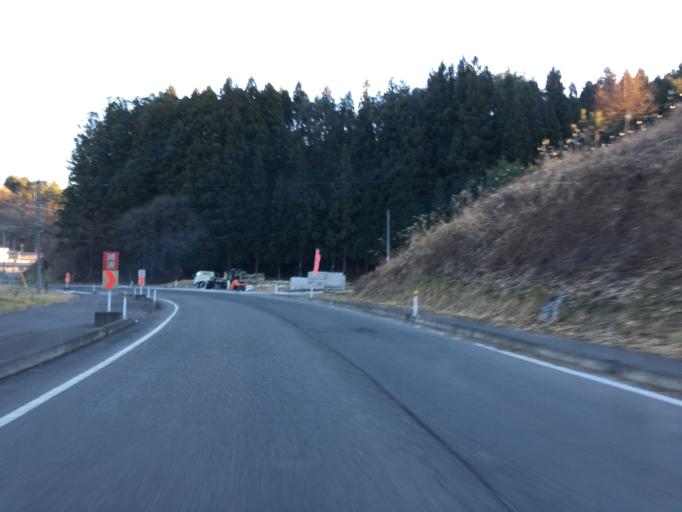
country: JP
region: Fukushima
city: Ishikawa
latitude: 37.1902
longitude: 140.5618
